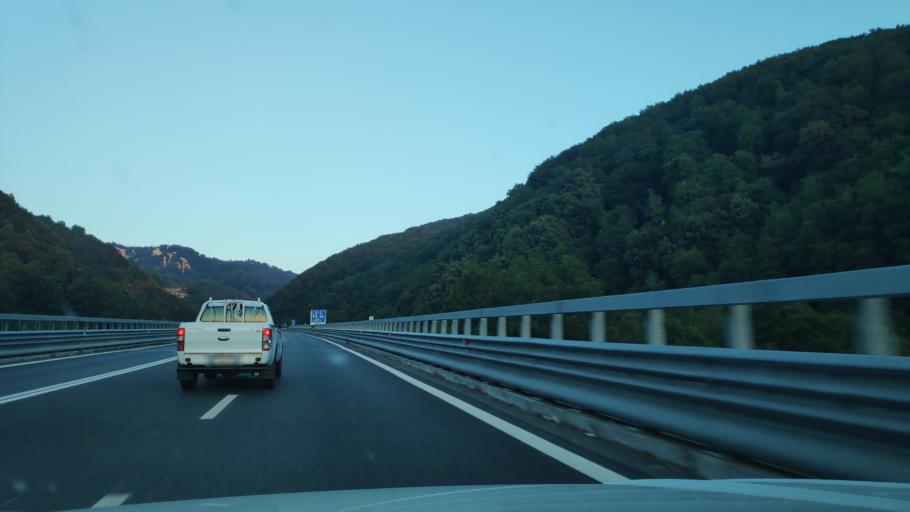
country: IT
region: Calabria
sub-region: Provincia di Reggio Calabria
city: Amato
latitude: 38.4056
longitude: 16.1520
